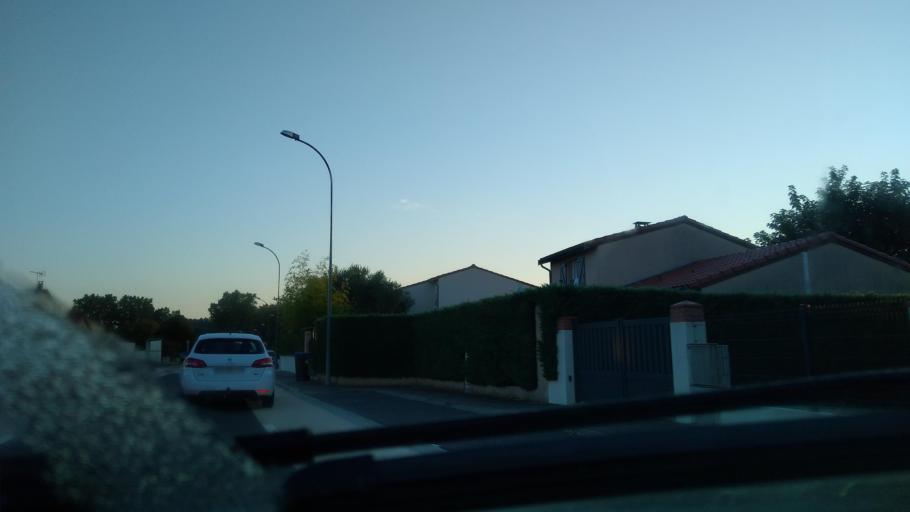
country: FR
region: Midi-Pyrenees
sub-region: Departement de la Haute-Garonne
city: Pibrac
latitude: 43.6143
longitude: 1.2896
